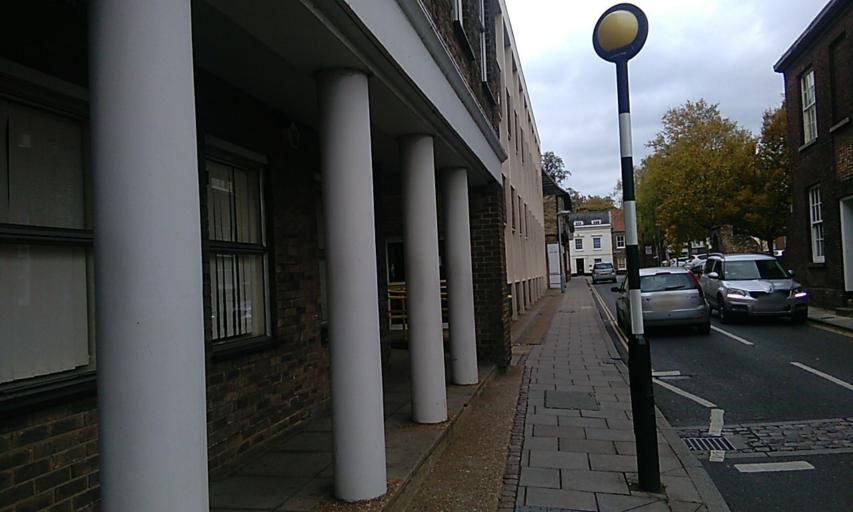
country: GB
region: England
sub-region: Norfolk
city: King's Lynn
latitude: 52.7570
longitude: 0.3949
